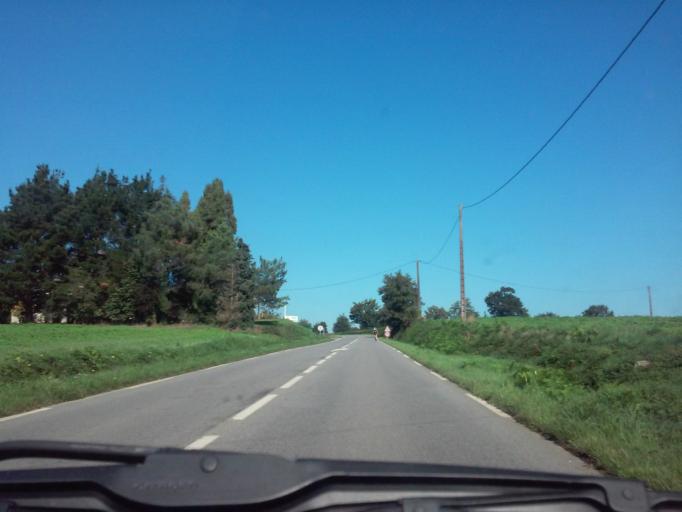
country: FR
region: Brittany
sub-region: Departement d'Ille-et-Vilaine
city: Chevaigne
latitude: 48.1981
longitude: -1.6259
